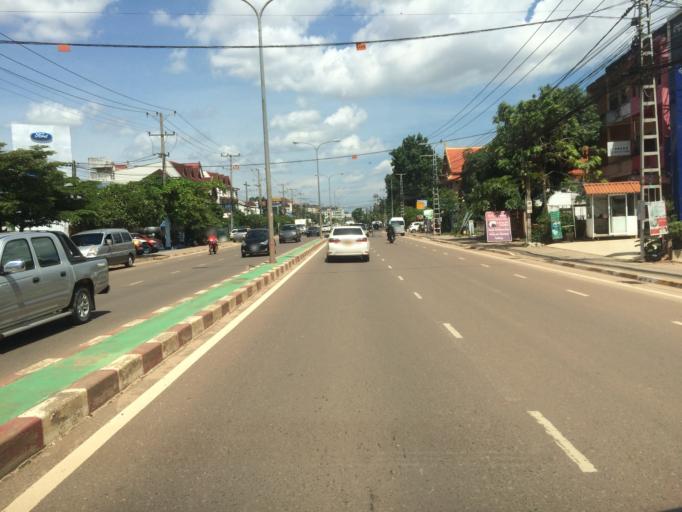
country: LA
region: Vientiane
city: Vientiane
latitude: 17.9688
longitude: 102.5904
